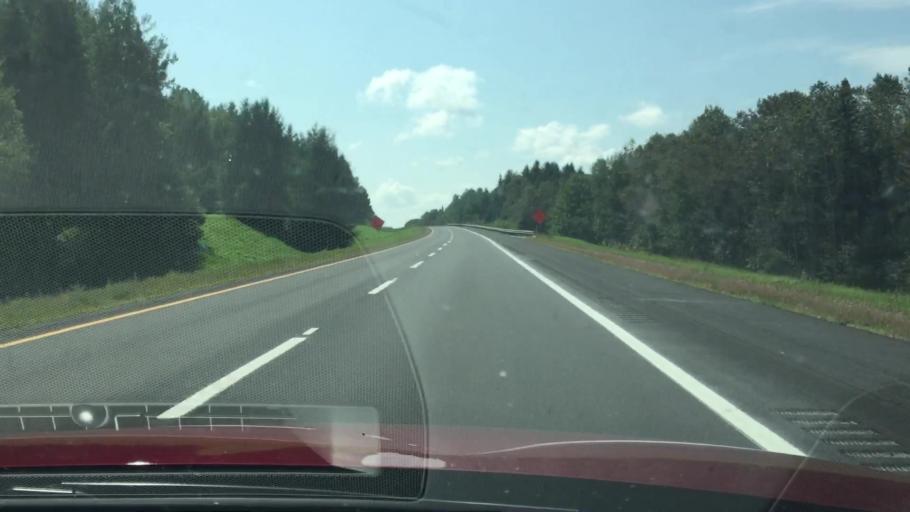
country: US
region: Maine
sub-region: Penobscot County
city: Patten
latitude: 45.9151
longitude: -68.3752
